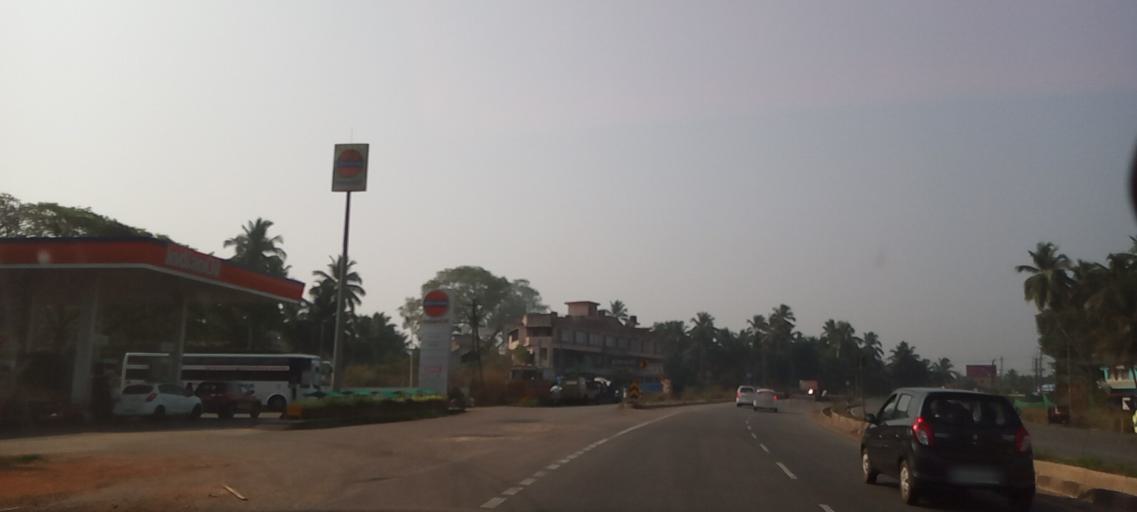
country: IN
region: Karnataka
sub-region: Udupi
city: Coondapoor
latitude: 13.6345
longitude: 74.7016
